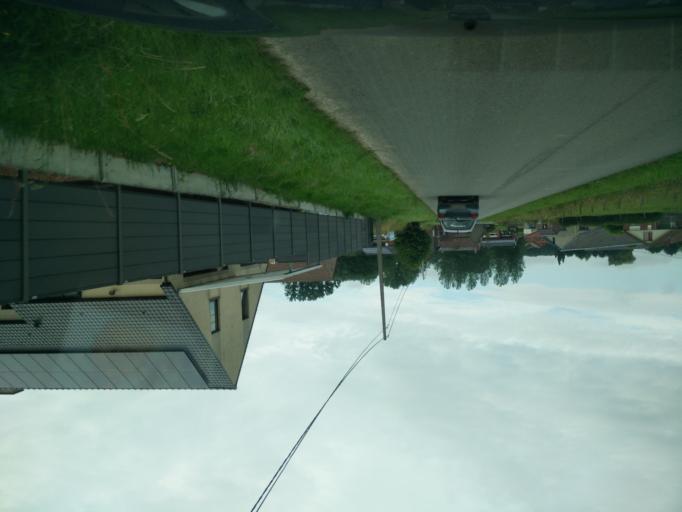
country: BE
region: Wallonia
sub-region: Province du Hainaut
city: Flobecq
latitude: 50.7451
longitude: 3.7365
